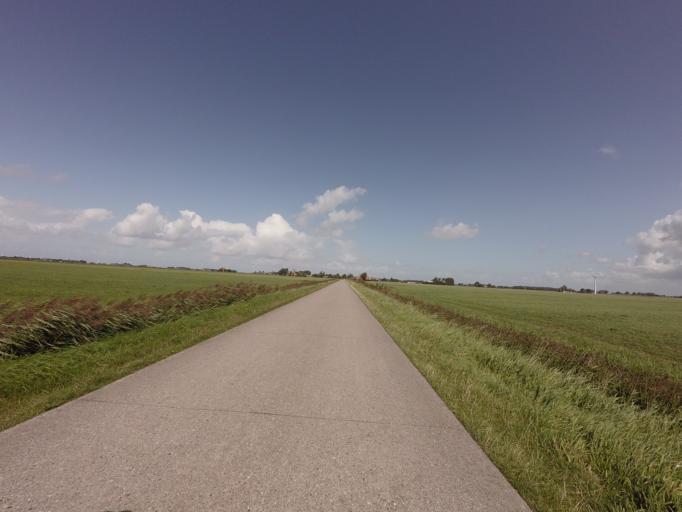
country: NL
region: Friesland
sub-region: Sudwest Fryslan
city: Makkum
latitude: 53.0713
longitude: 5.4540
